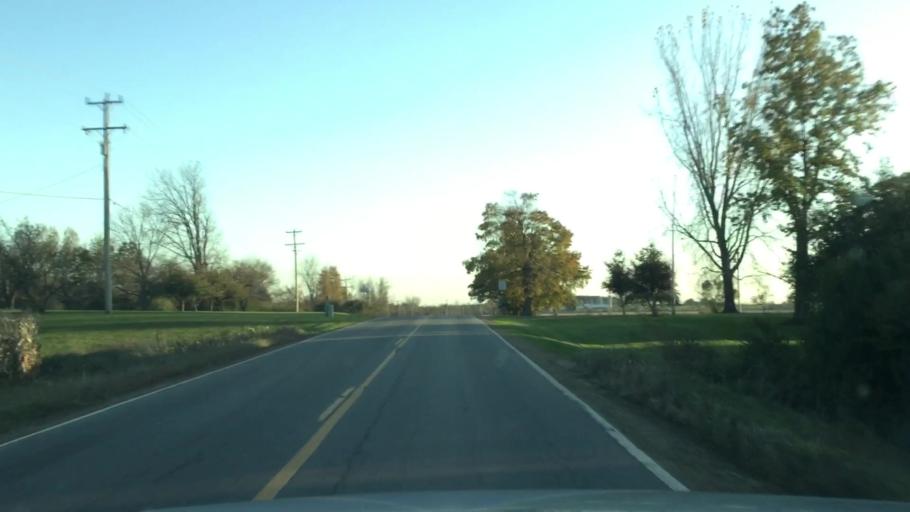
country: US
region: Michigan
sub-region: Lapeer County
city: North Branch
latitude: 43.3313
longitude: -83.1836
